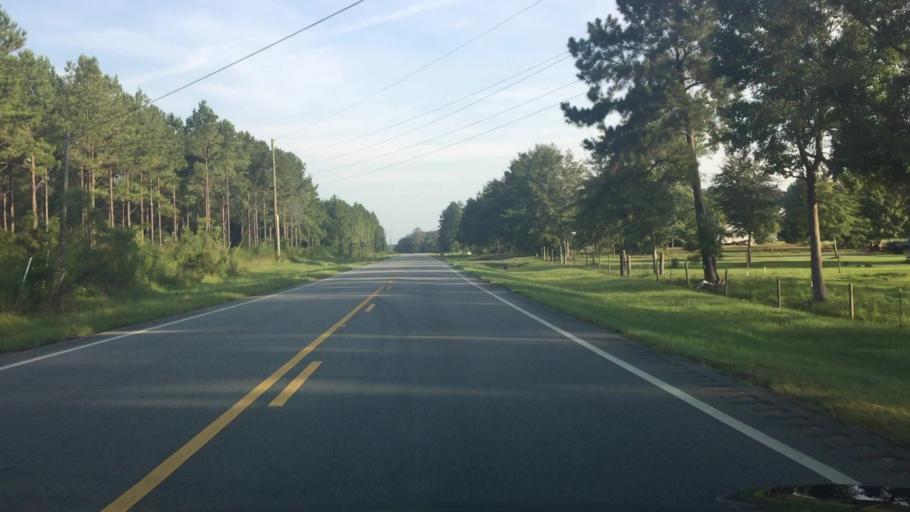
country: US
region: Alabama
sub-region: Covington County
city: Florala
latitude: 31.0183
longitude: -86.3622
